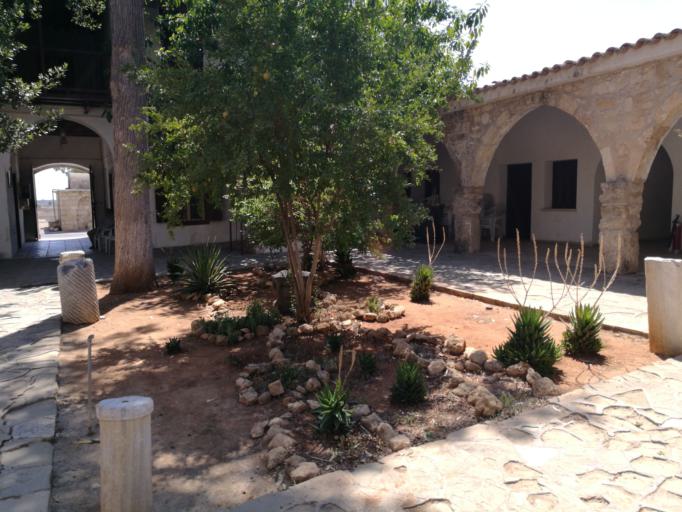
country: CY
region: Ammochostos
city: Acheritou
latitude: 35.1747
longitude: 33.8803
